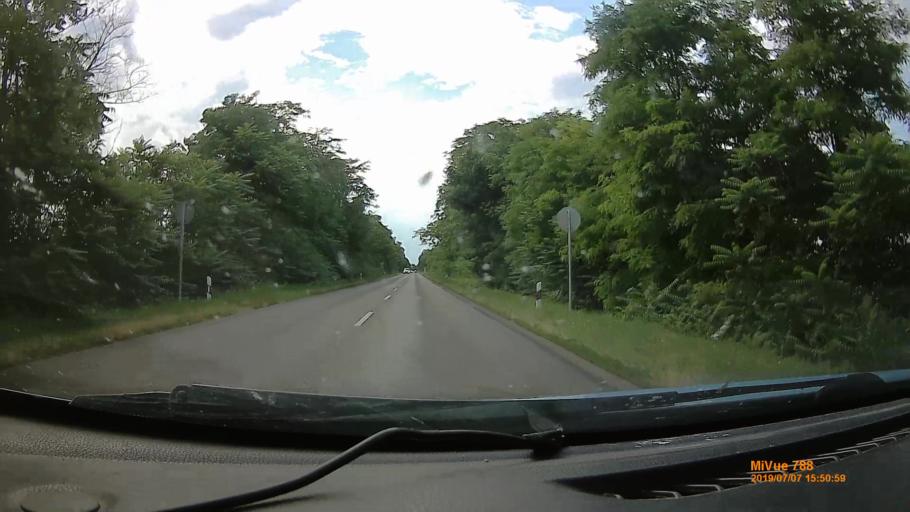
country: HU
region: Jasz-Nagykun-Szolnok
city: Jaszbereny
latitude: 47.5299
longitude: 19.8465
